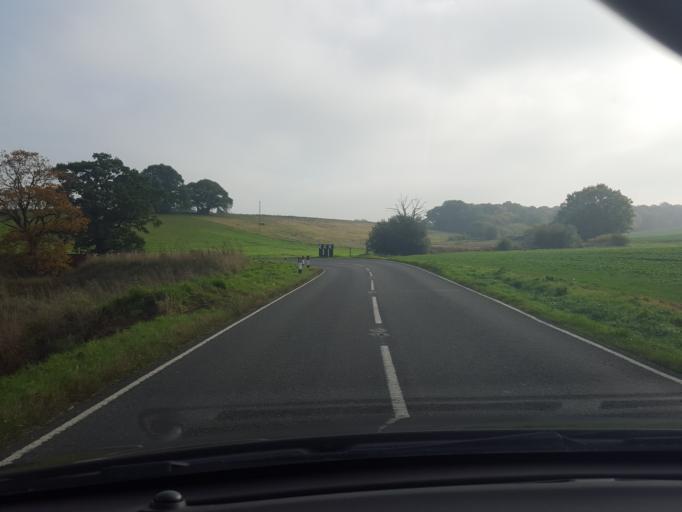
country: GB
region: England
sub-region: Essex
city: Mistley
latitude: 51.9390
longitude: 1.1072
